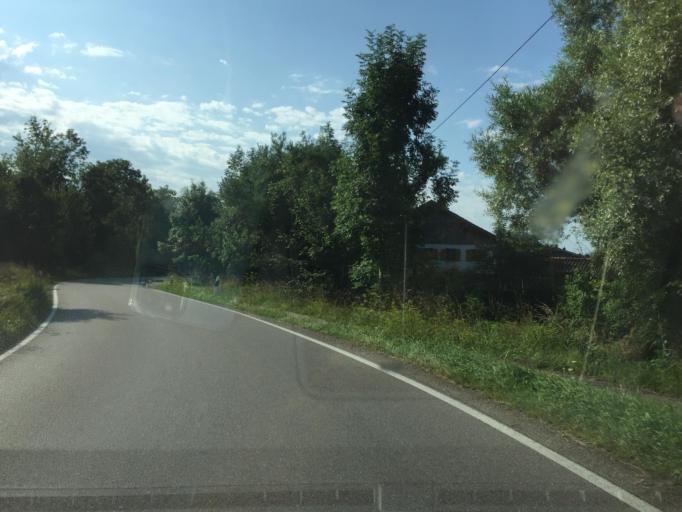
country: DE
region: Bavaria
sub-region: Upper Bavaria
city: Tuntenhausen
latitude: 47.9567
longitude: 12.0174
